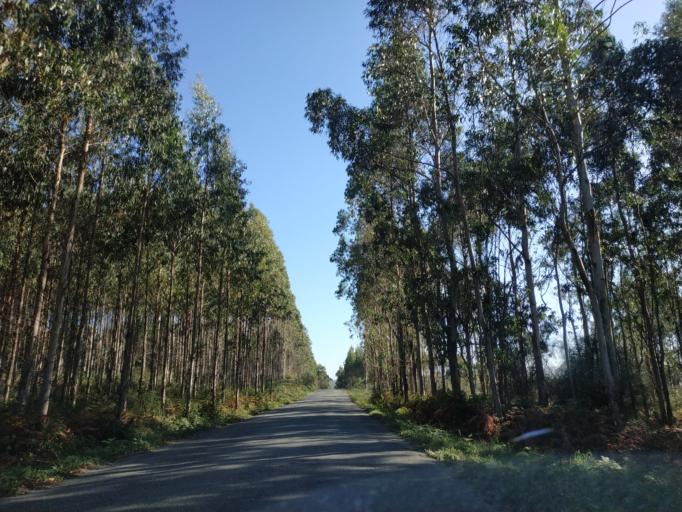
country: ES
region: Galicia
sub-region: Provincia da Coruna
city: Santa Comba
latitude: 43.0192
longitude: -8.7412
